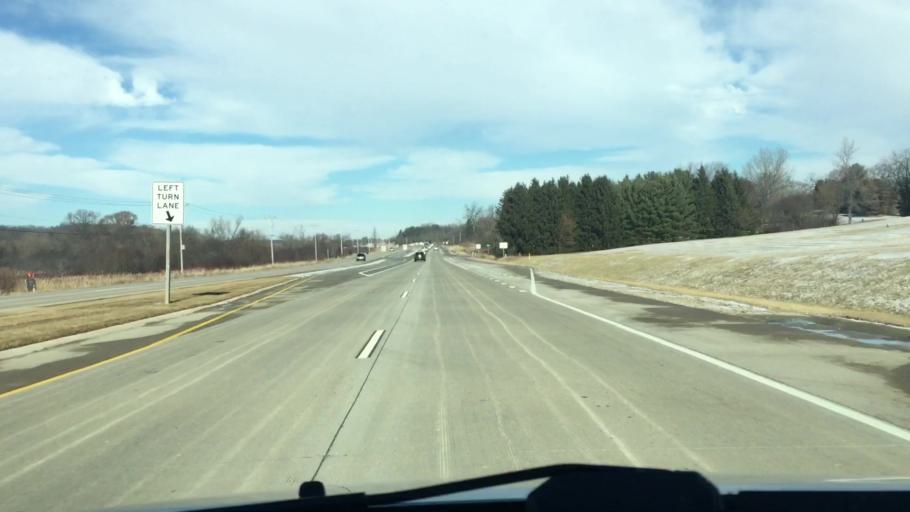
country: US
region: Wisconsin
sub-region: Waukesha County
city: Mukwonago
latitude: 42.8905
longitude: -88.3436
